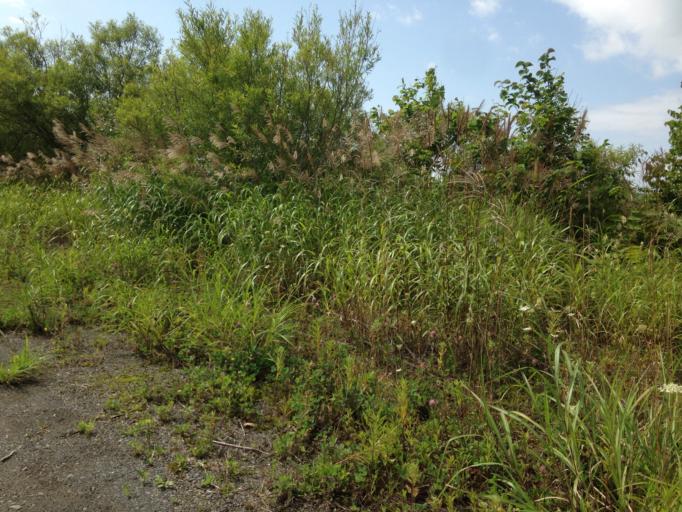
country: JP
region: Hokkaido
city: Tobetsu
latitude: 43.2577
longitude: 141.5292
